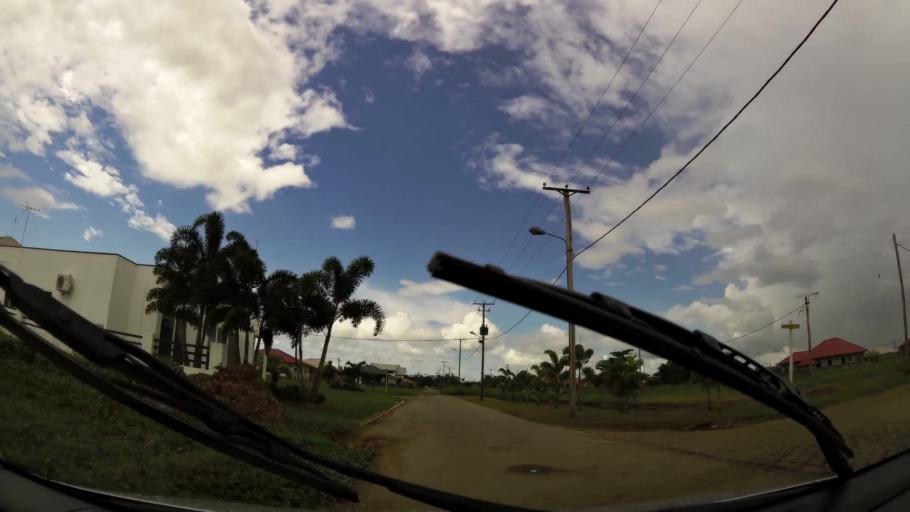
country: SR
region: Paramaribo
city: Paramaribo
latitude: 5.8638
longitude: -55.1234
